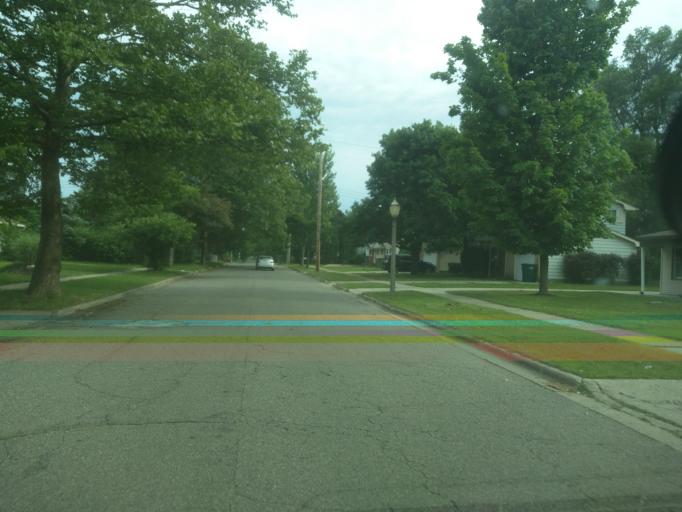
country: US
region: Michigan
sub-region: Eaton County
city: Waverly
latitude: 42.6928
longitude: -84.5965
